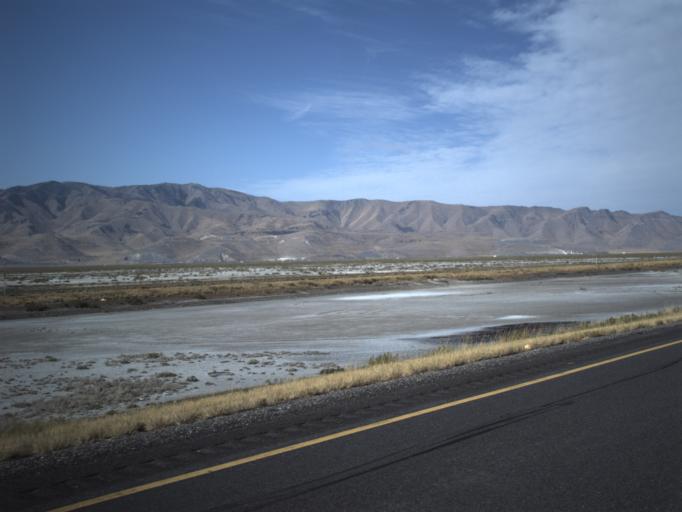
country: US
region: Utah
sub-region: Tooele County
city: Grantsville
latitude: 40.6959
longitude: -112.4745
